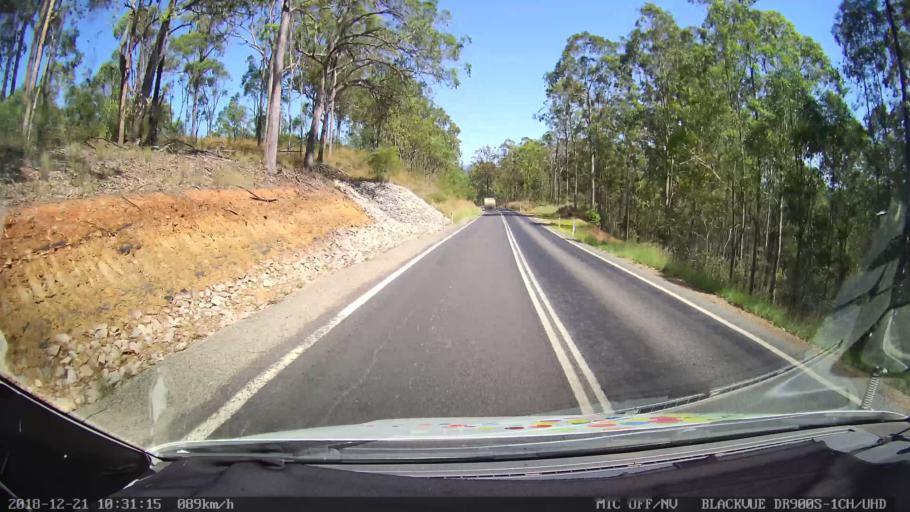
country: AU
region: New South Wales
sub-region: Clarence Valley
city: South Grafton
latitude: -29.6329
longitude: 152.6983
